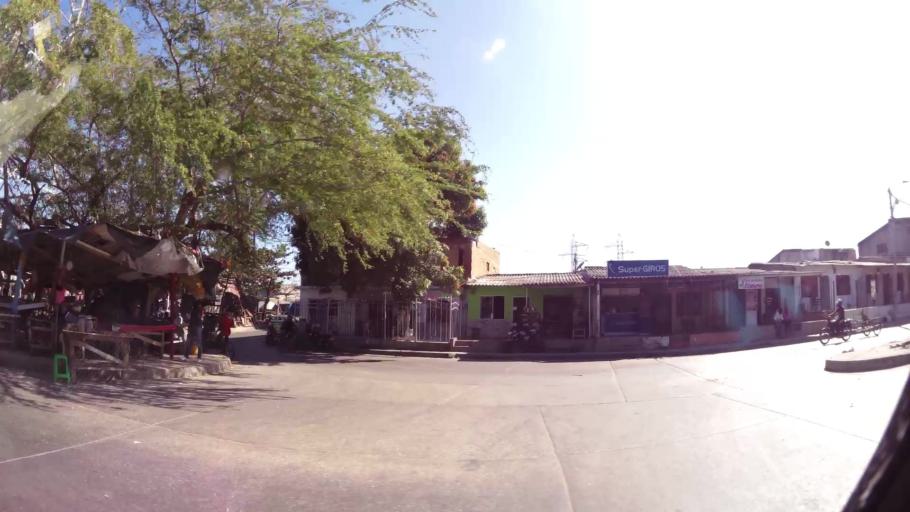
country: CO
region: Atlantico
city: Soledad
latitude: 10.9294
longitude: -74.7927
